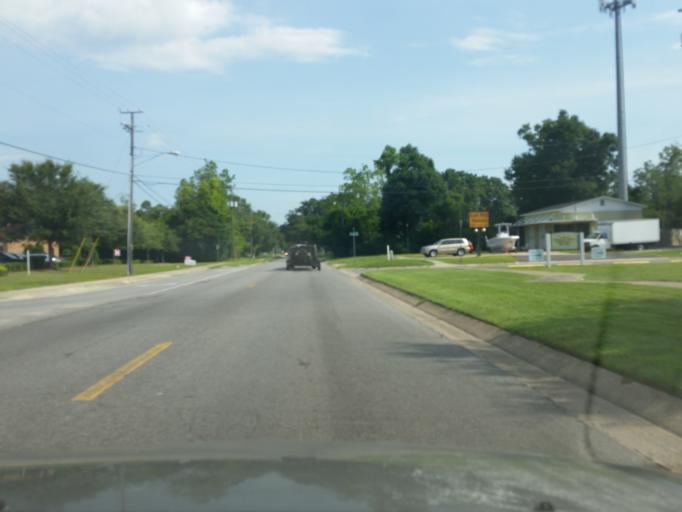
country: US
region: Florida
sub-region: Escambia County
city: Goulding
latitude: 30.4473
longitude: -87.2079
